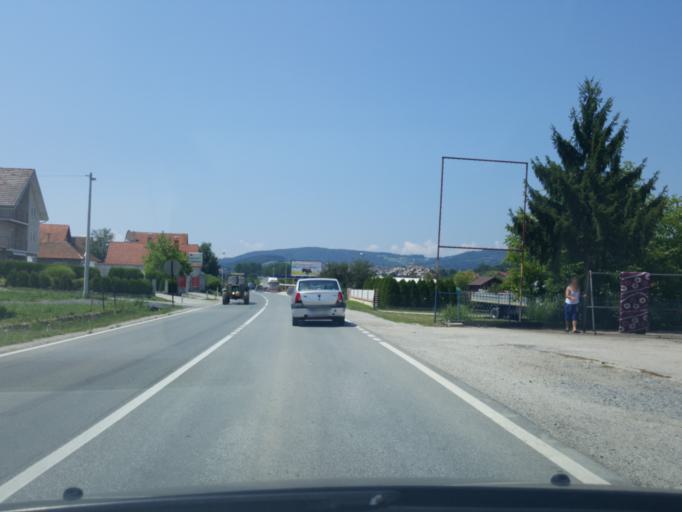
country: RS
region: Central Serbia
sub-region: Moravicki Okrug
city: Gornji Milanovac
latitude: 44.0335
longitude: 20.4770
